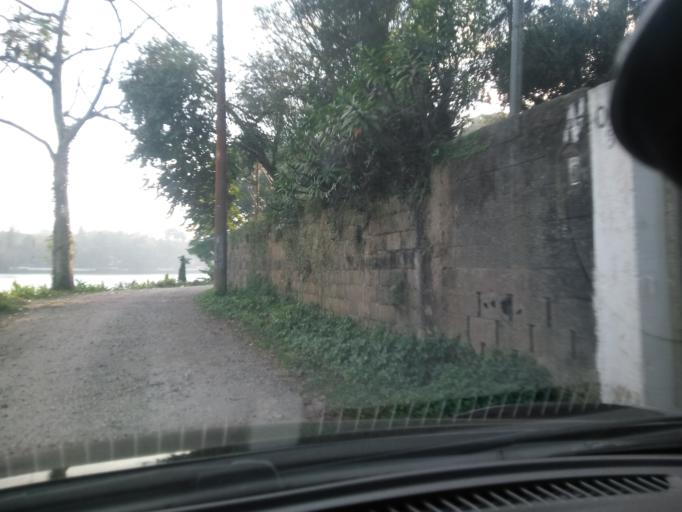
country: BR
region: Sao Paulo
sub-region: Sao Bernardo Do Campo
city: Sao Bernardo do Campo
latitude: -23.7892
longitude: -46.5395
